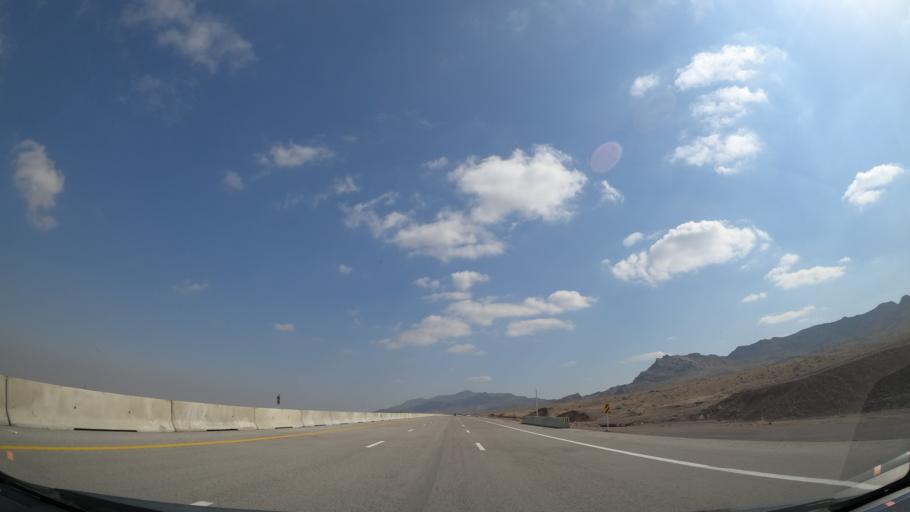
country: IR
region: Alborz
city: Eshtehard
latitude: 35.7085
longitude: 50.6023
